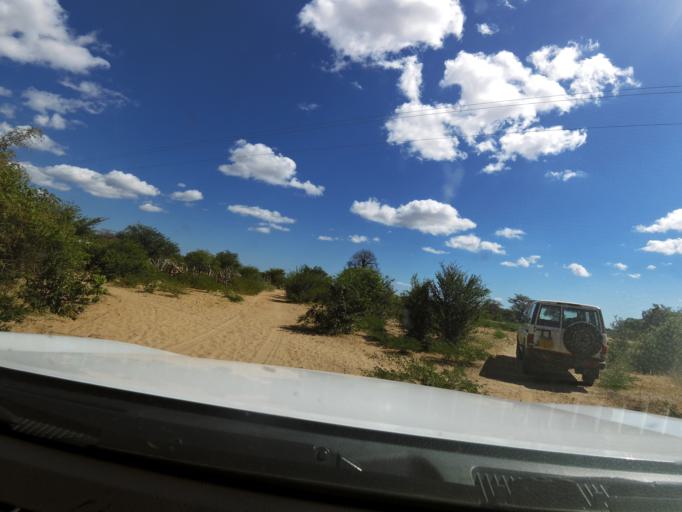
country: ZW
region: Matabeleland North
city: Kamativi Mine
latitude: -18.0053
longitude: 27.1446
